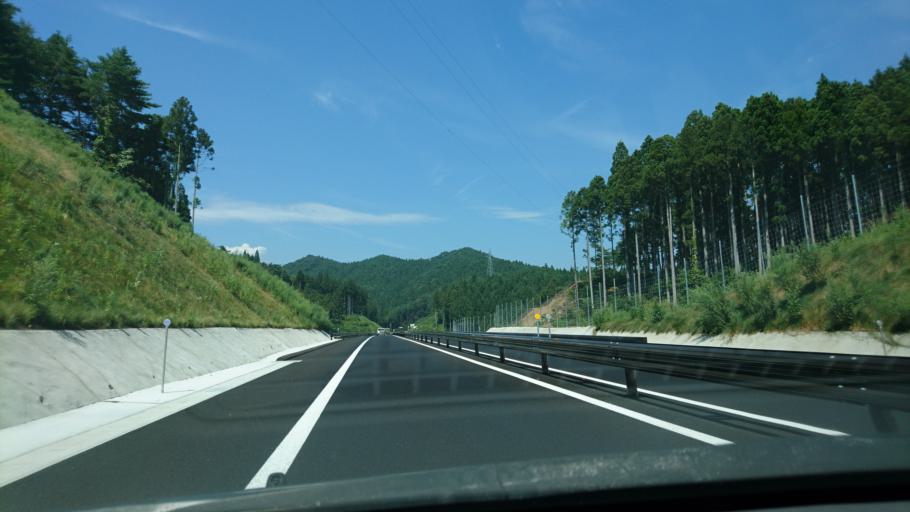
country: JP
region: Iwate
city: Ofunato
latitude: 39.0126
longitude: 141.6092
